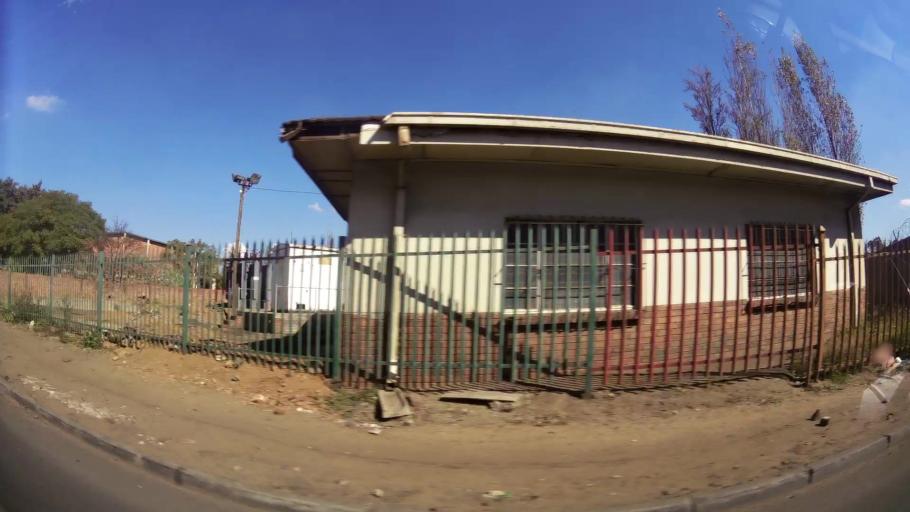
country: ZA
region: Mpumalanga
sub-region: Nkangala District Municipality
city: Witbank
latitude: -25.8755
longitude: 29.2076
